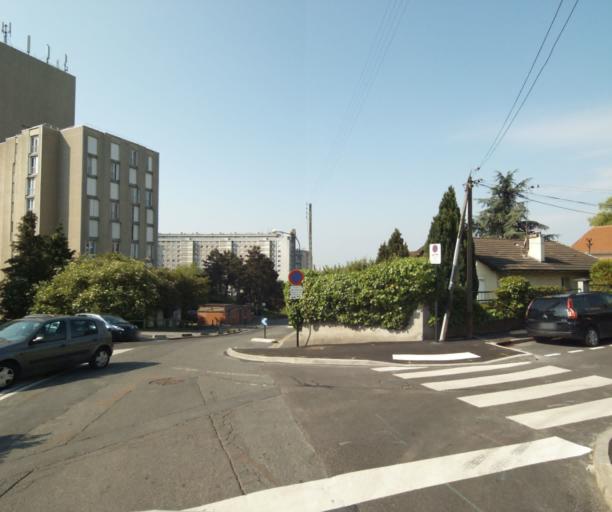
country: FR
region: Ile-de-France
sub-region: Departement du Val-d'Oise
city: Sannois
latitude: 48.9636
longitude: 2.2471
